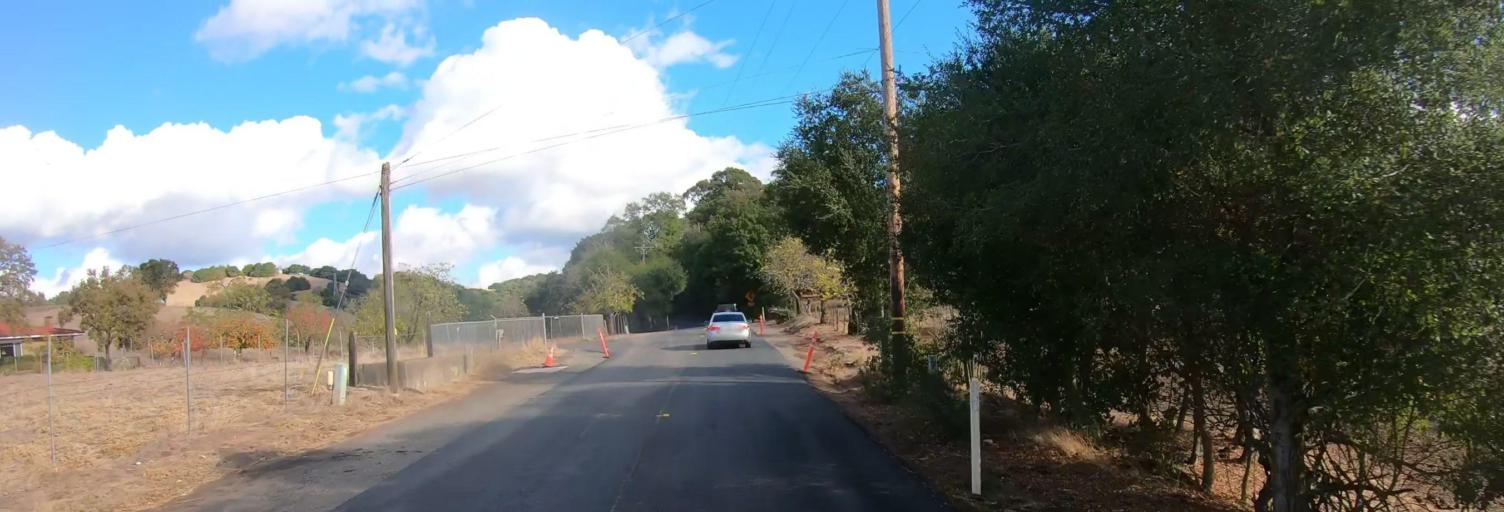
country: US
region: California
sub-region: Santa Clara County
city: East Foothills
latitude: 37.3631
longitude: -121.7586
